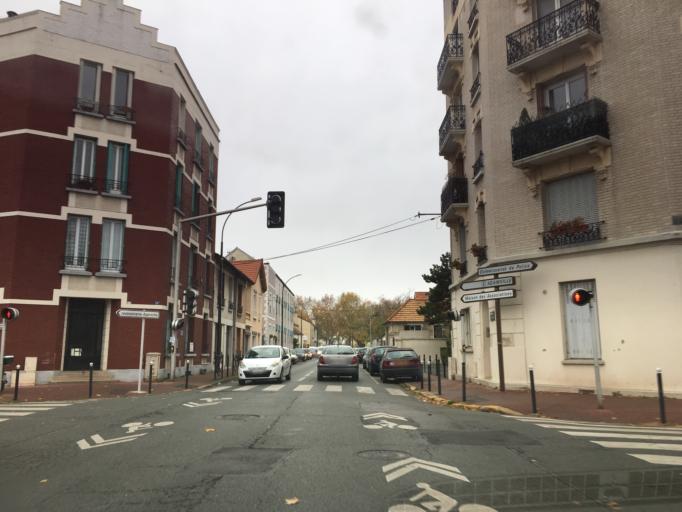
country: FR
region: Ile-de-France
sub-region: Departement du Val-de-Marne
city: Saint-Maur-des-Fosses
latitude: 48.7938
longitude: 2.4899
